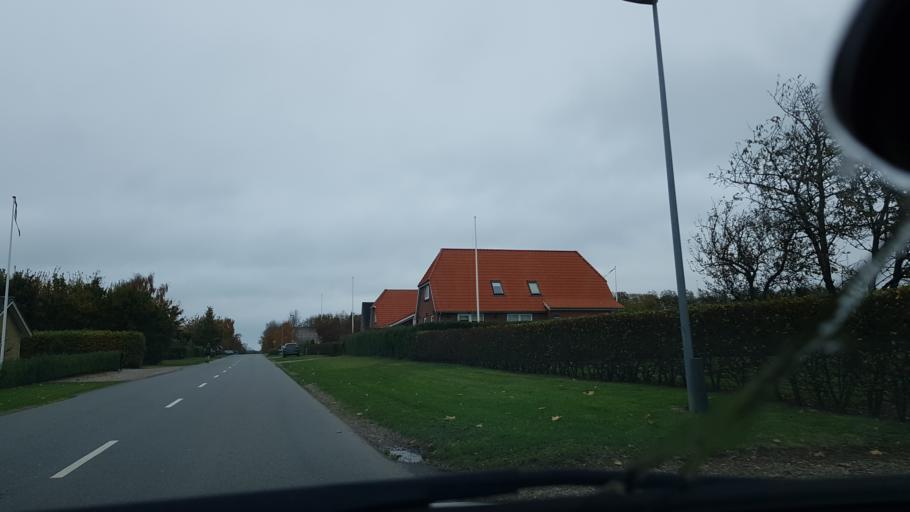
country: DK
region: South Denmark
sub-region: Esbjerg Kommune
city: Ribe
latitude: 55.2485
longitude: 8.8279
